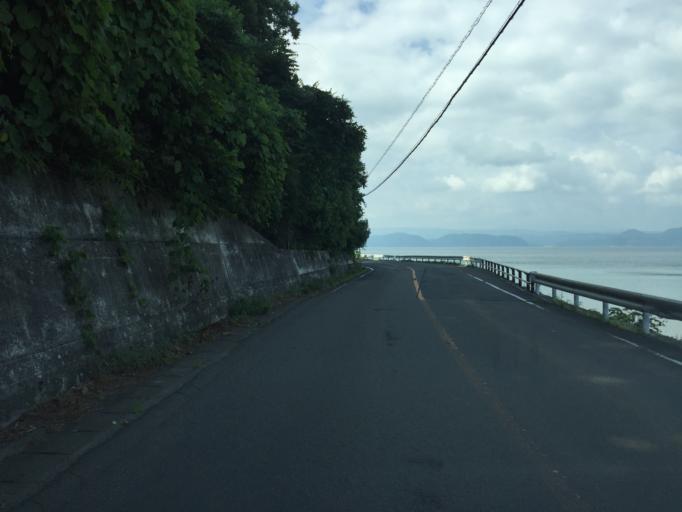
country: JP
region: Fukushima
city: Inawashiro
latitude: 37.4595
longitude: 140.1538
